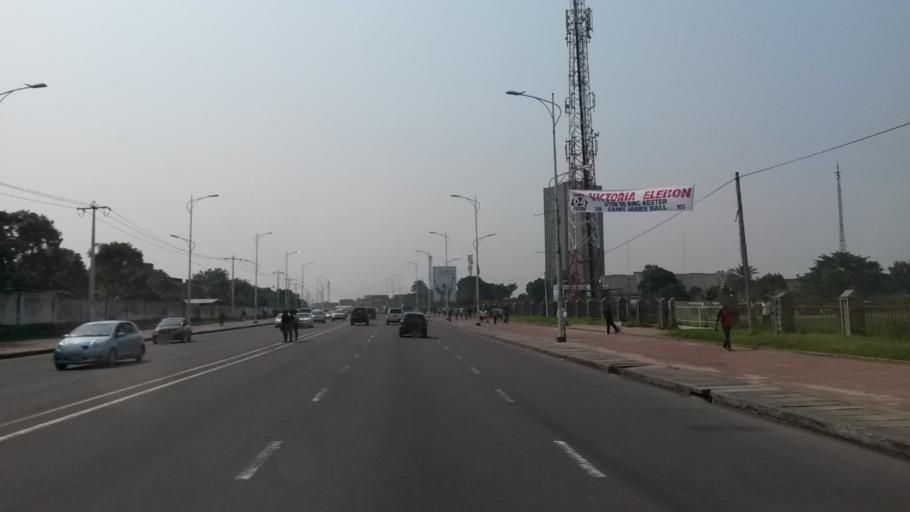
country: CD
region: Kinshasa
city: Kinshasa
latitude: -4.3332
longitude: 15.2965
